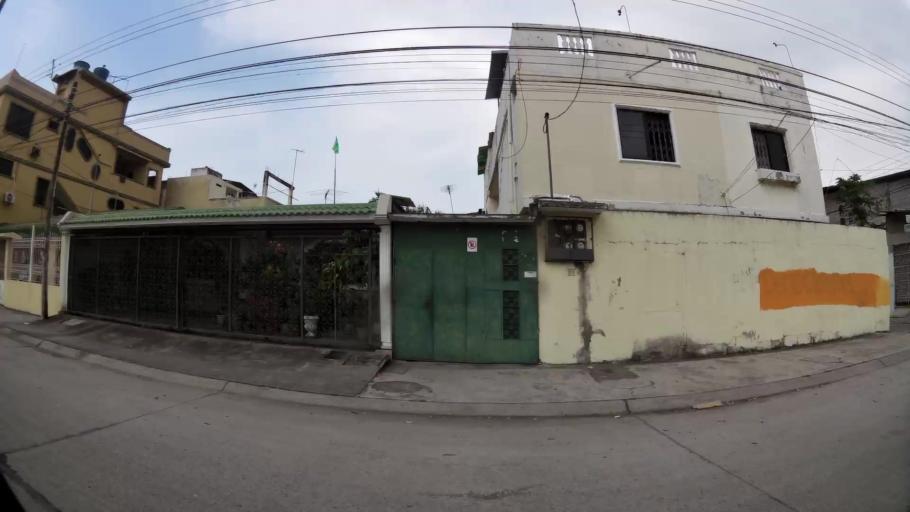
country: EC
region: Guayas
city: Eloy Alfaro
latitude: -2.1176
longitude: -79.8927
